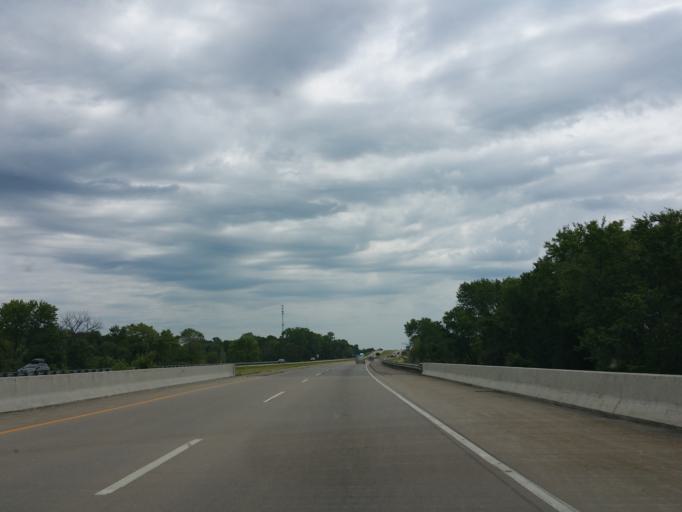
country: US
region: Wisconsin
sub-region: Juneau County
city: New Lisbon
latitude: 43.8917
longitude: -90.1651
